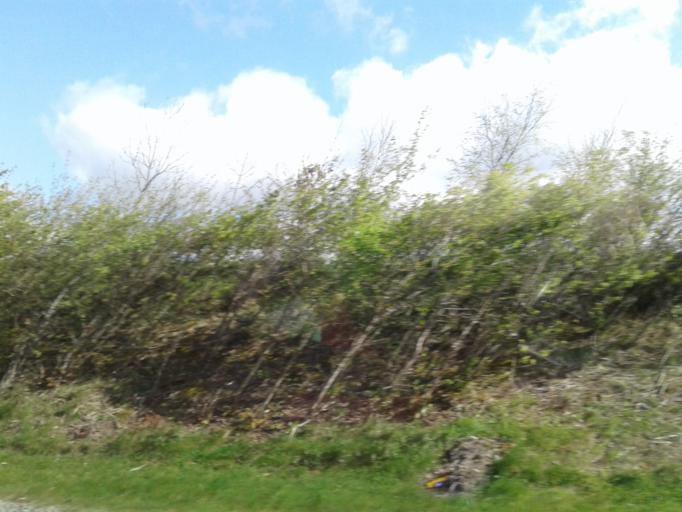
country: IE
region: Leinster
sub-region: An Mhi
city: Ashbourne
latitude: 53.4620
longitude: -6.3569
